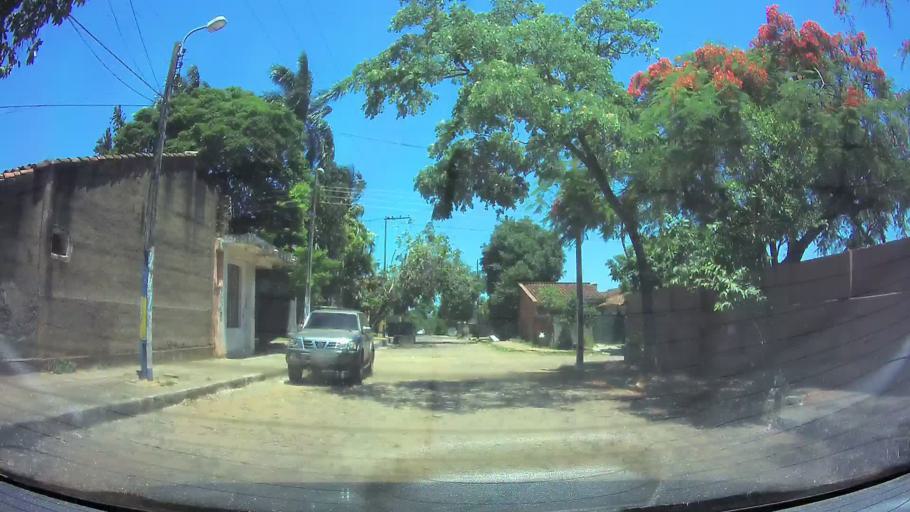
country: PY
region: Central
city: San Lorenzo
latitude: -25.2604
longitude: -57.4896
